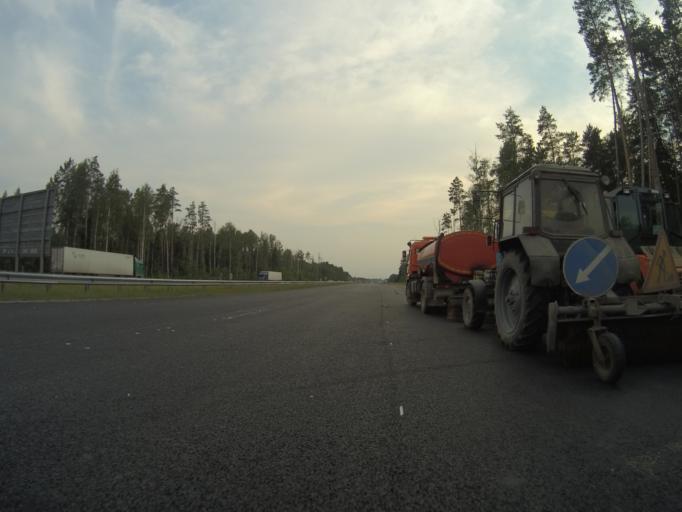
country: RU
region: Vladimir
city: Sudogda
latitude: 56.1386
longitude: 40.8939
